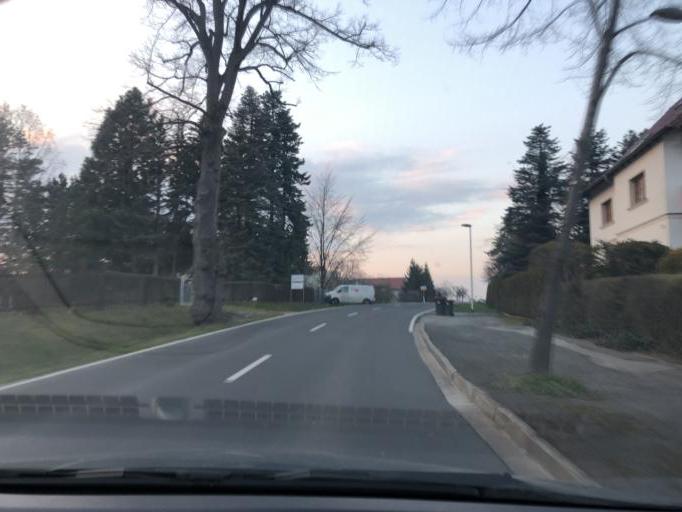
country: DE
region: Saxony
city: Elstra
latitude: 51.2248
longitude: 14.1312
